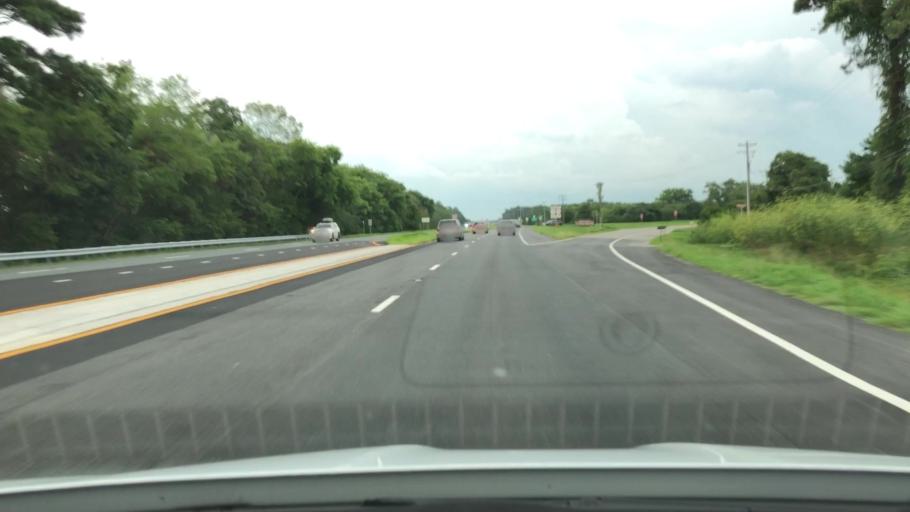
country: US
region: Virginia
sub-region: Northampton County
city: Cape Charles
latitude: 37.1792
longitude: -75.9690
